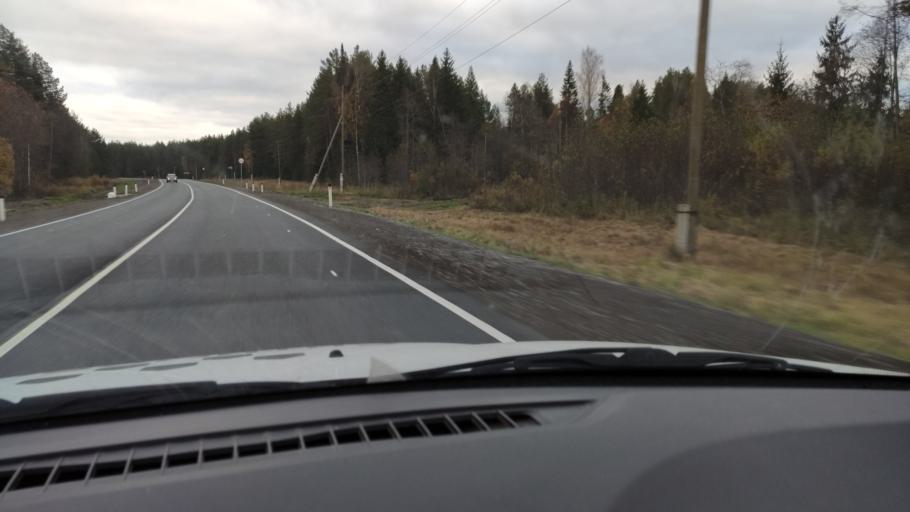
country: RU
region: Kirov
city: Belaya Kholunitsa
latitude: 58.8421
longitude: 50.7733
